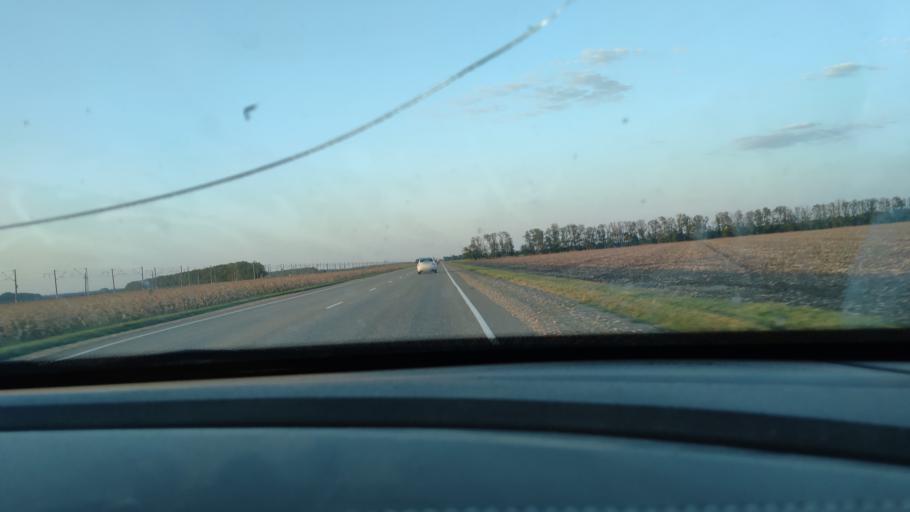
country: RU
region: Krasnodarskiy
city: Novominskaya
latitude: 46.3748
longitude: 38.9783
